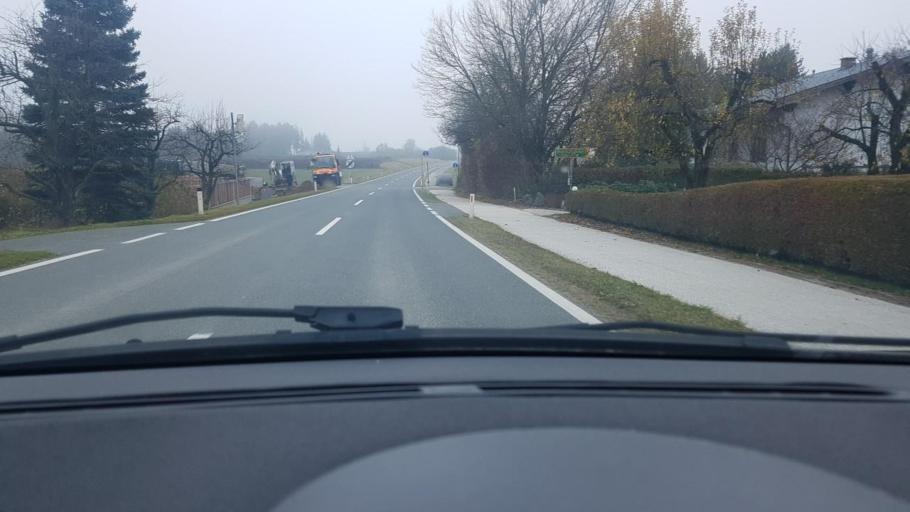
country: AT
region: Carinthia
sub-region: Politischer Bezirk Volkermarkt
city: Bleiburg/Pliberk
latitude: 46.6105
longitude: 14.8001
